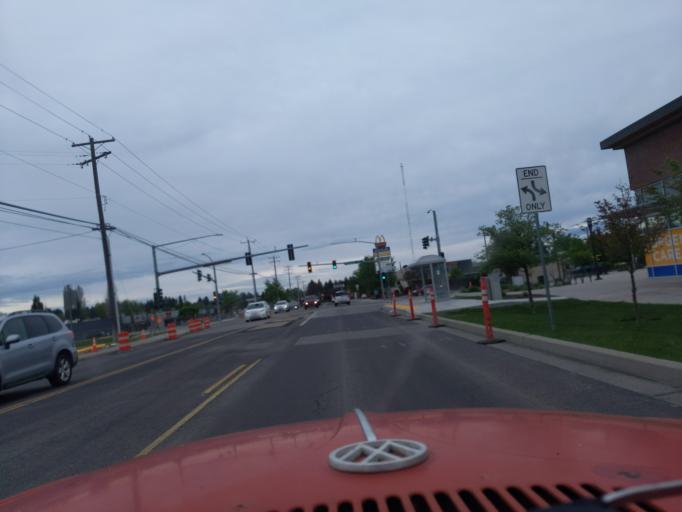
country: US
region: Washington
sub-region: Spokane County
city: Spokane
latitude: 47.6096
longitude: -117.3682
